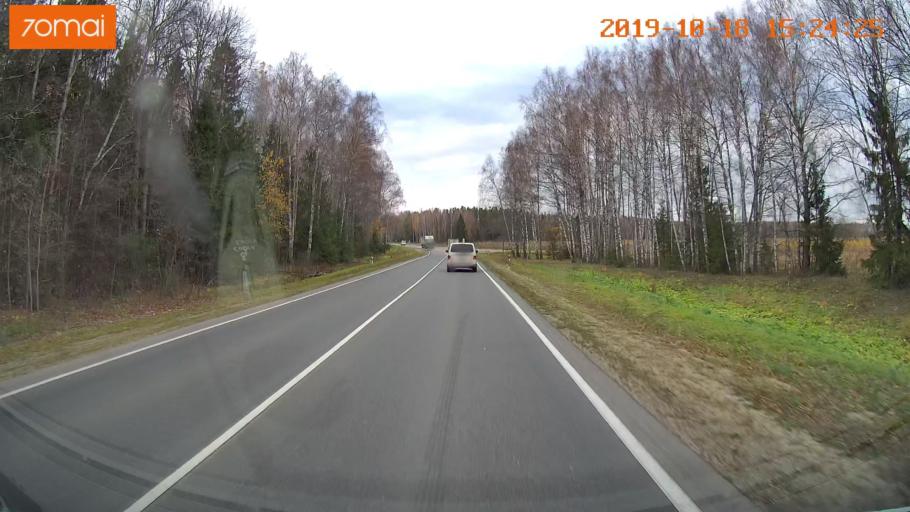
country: RU
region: Vladimir
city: Anopino
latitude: 55.7340
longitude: 40.7232
